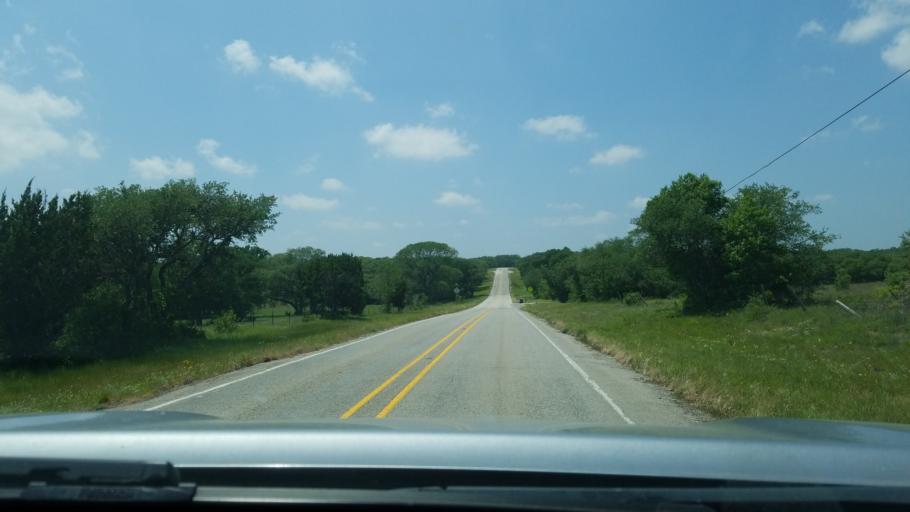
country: US
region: Texas
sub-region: Hays County
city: Woodcreek
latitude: 30.0988
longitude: -98.2518
